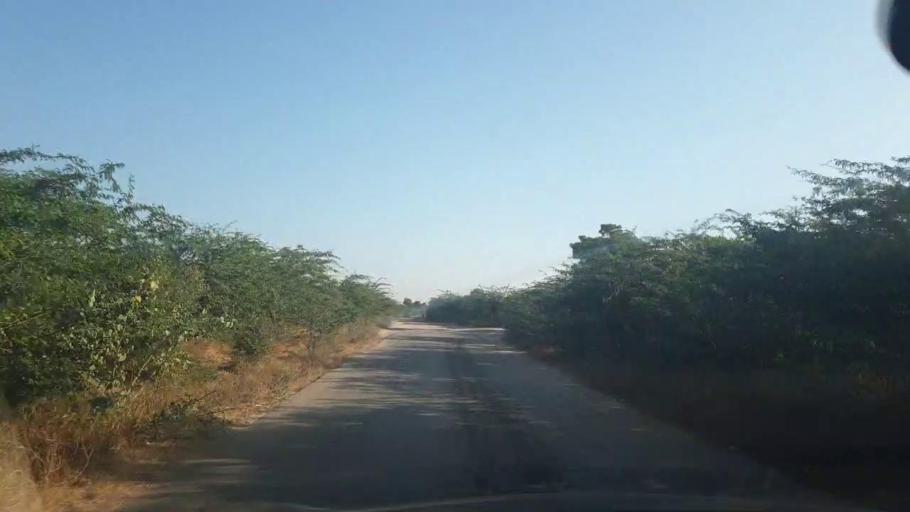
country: PK
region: Sindh
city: Malir Cantonment
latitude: 25.1074
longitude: 67.2621
